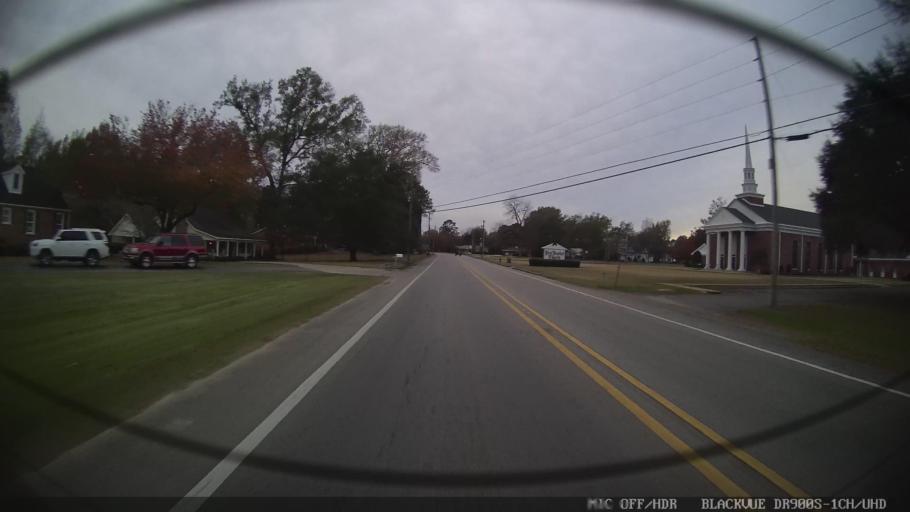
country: US
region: Mississippi
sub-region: Clarke County
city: Quitman
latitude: 32.0382
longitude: -88.7184
